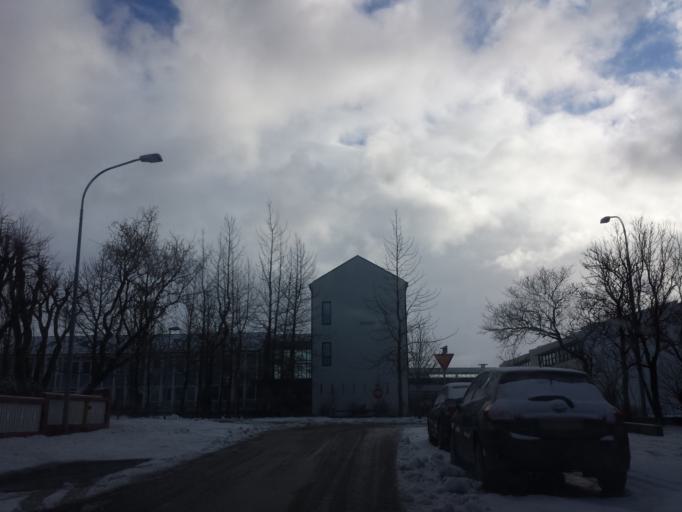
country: IS
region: Capital Region
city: Reykjavik
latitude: 64.1372
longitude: -21.9048
